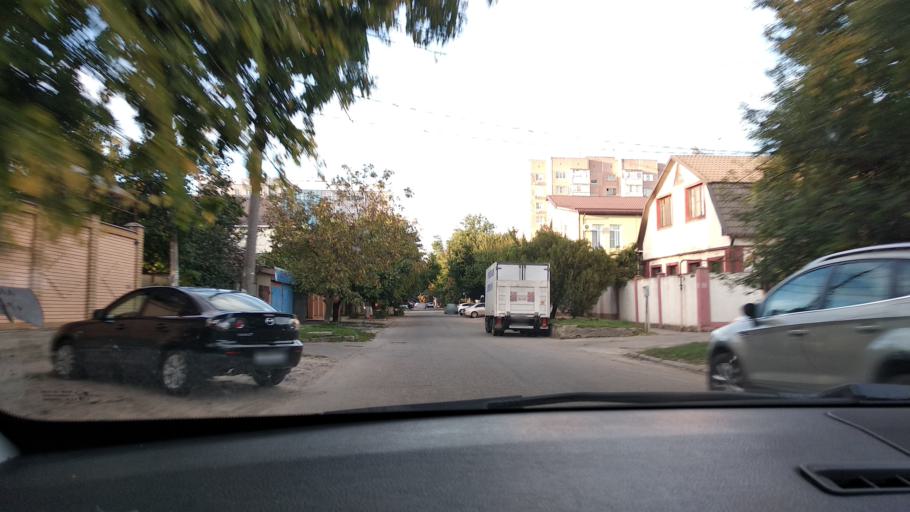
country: RU
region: Krasnodarskiy
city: Krasnodar
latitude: 45.0180
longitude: 39.0044
